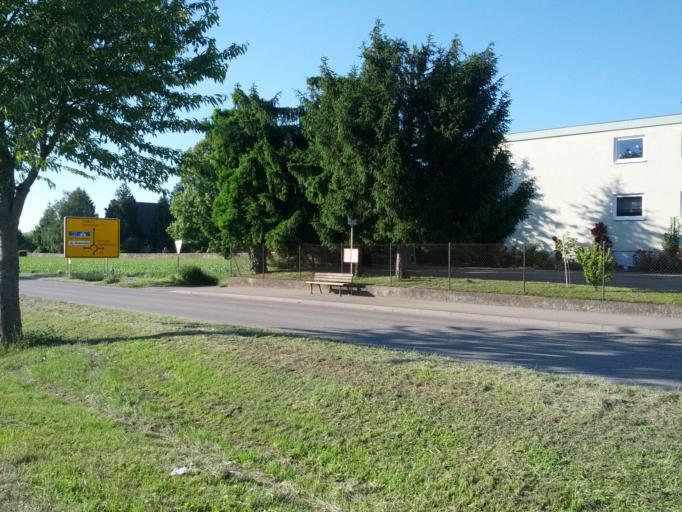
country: DE
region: Baden-Wuerttemberg
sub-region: Freiburg Region
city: Pfaffenweiler
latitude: 47.9233
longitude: 7.7365
